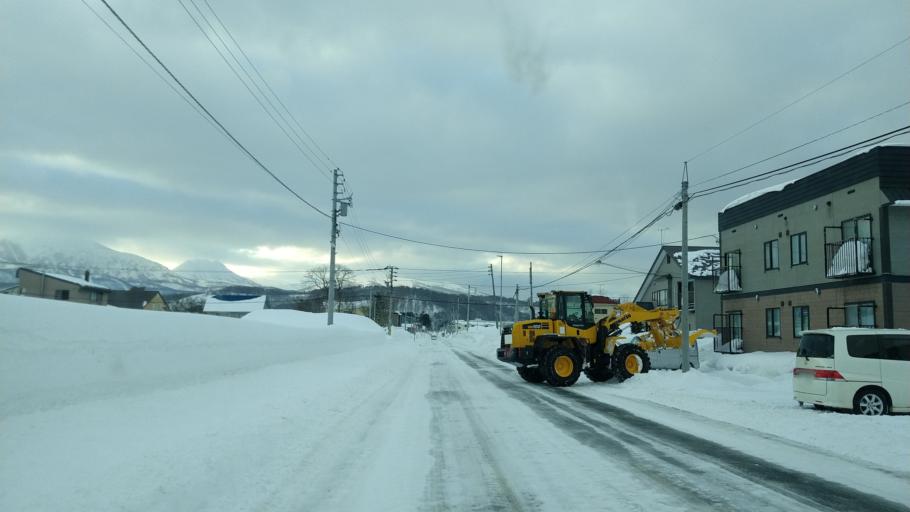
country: JP
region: Hokkaido
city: Niseko Town
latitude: 42.9086
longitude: 140.7612
